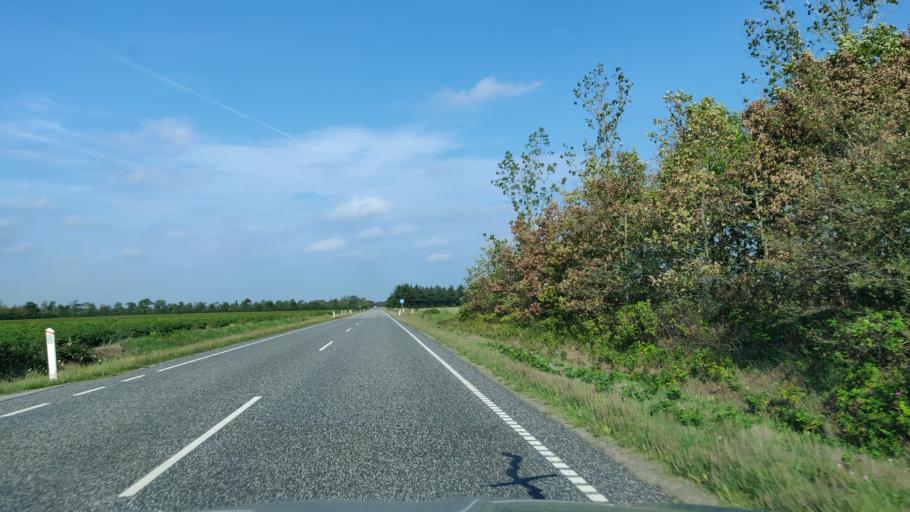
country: DK
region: Central Jutland
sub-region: Herning Kommune
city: Sunds
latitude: 56.2496
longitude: 9.0603
